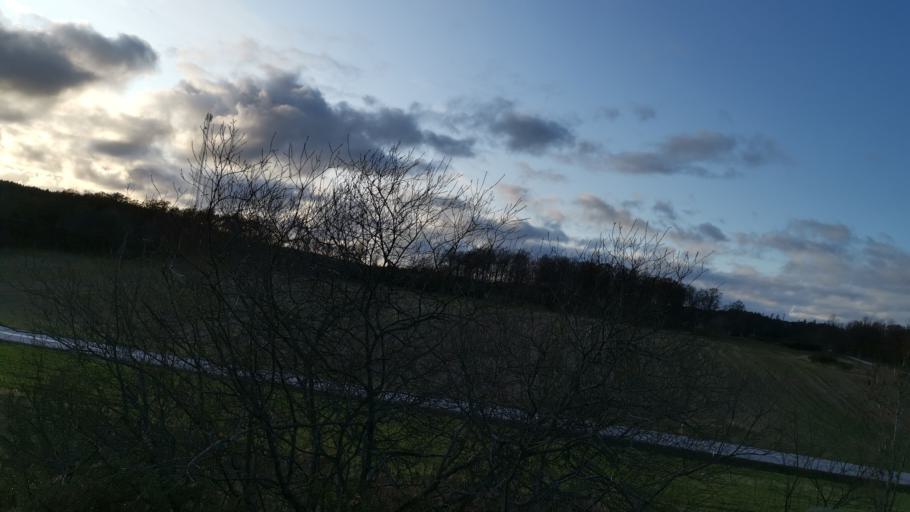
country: SE
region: Vaestra Goetaland
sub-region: Munkedals Kommun
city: Munkedal
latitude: 58.4667
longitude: 11.6602
